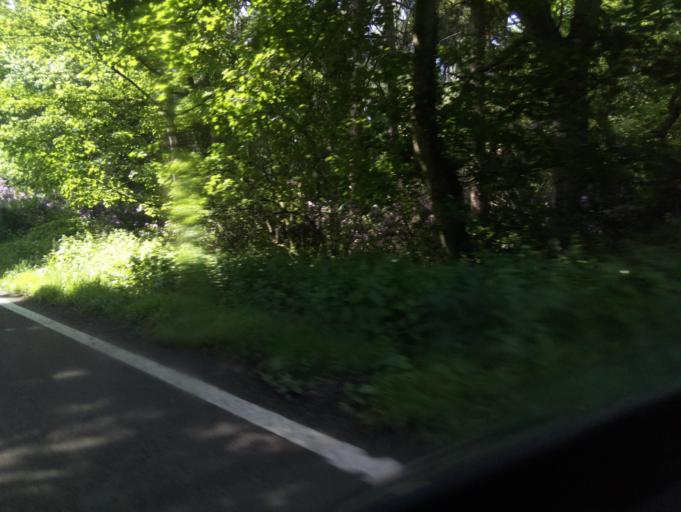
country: GB
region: England
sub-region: North Lincolnshire
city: Manton
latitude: 53.5395
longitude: -0.5768
